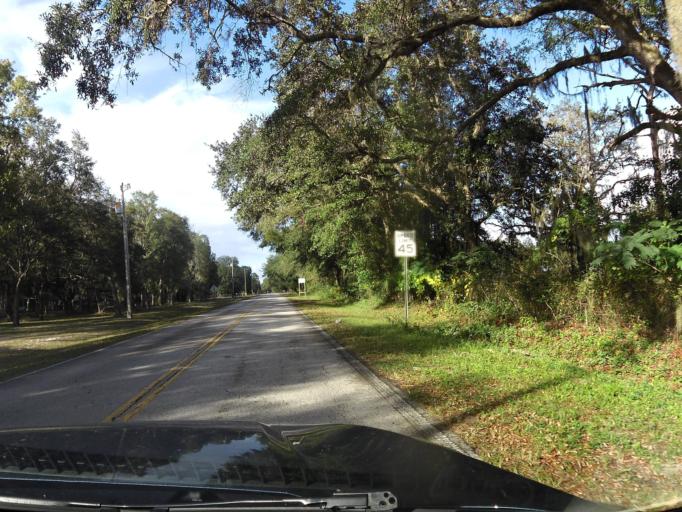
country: US
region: Florida
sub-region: Clay County
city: Asbury Lake
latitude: 29.9826
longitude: -81.8394
